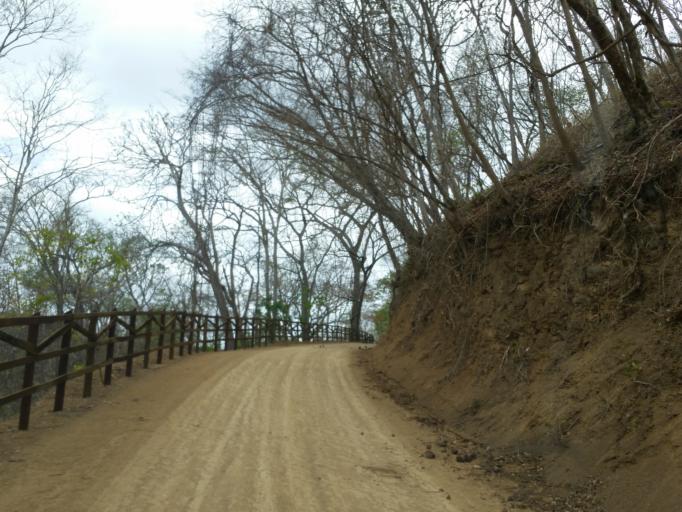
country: NI
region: Rivas
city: Tola
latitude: 11.4284
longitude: -86.0662
